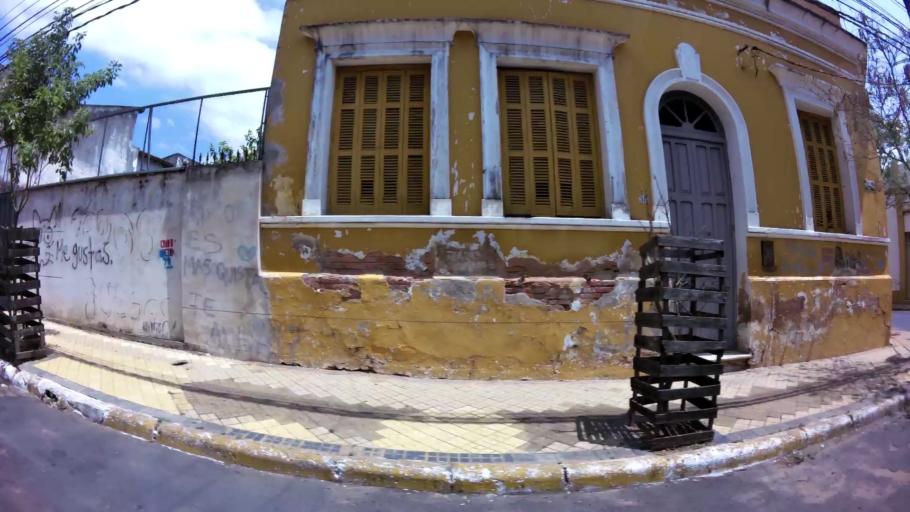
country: PY
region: Asuncion
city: Asuncion
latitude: -25.2893
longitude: -57.6339
